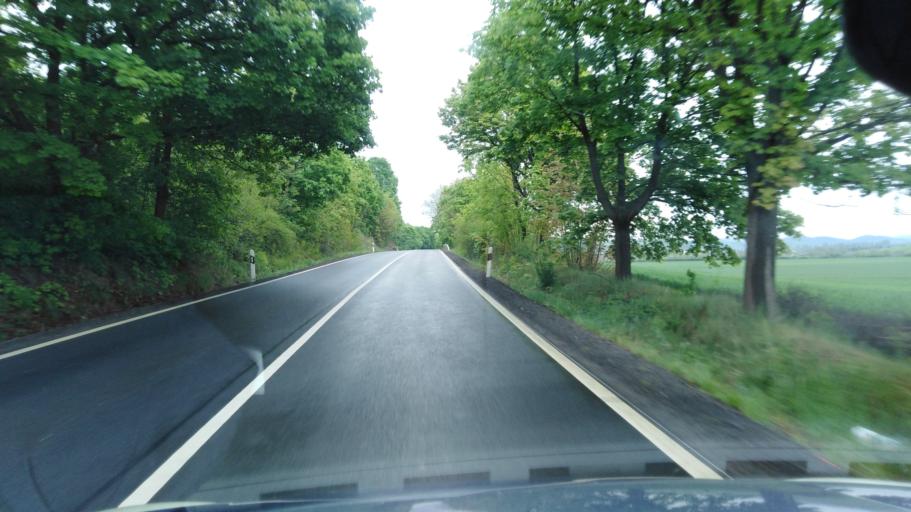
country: HU
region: Nograd
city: Karancskeszi
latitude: 48.1298
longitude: 19.6092
